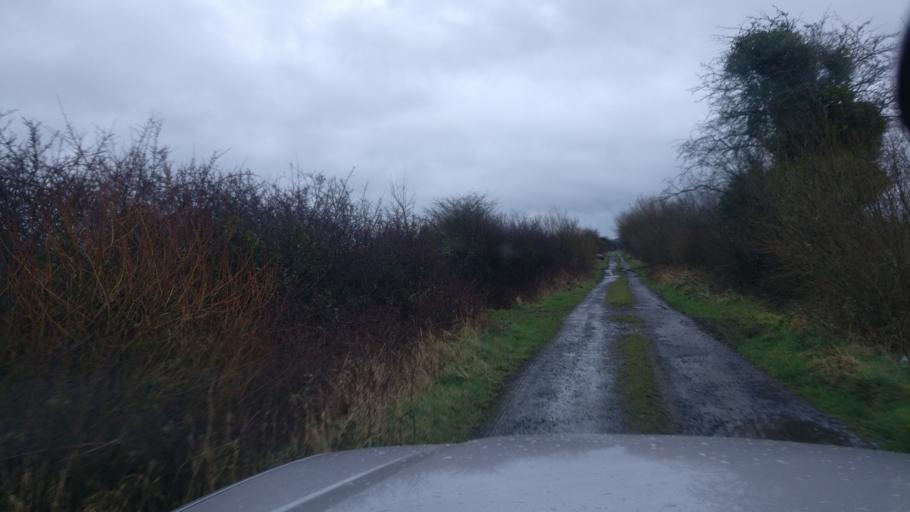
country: IE
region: Connaught
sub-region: County Galway
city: Ballinasloe
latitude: 53.2508
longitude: -8.3289
